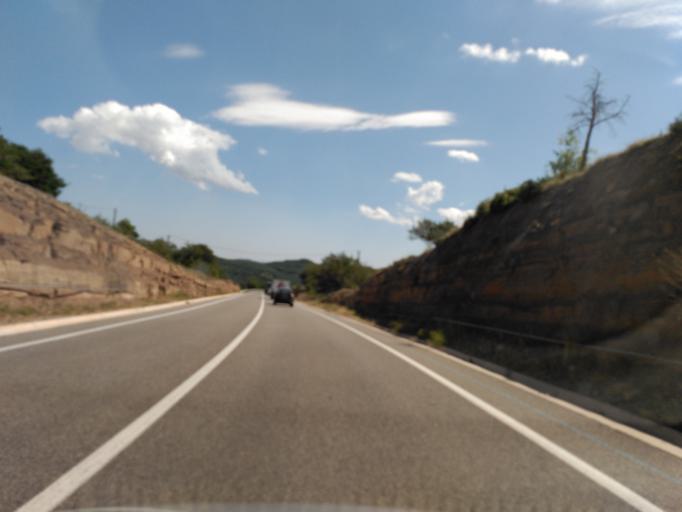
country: ES
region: Catalonia
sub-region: Provincia de Barcelona
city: Olost
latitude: 41.9412
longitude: 2.1406
